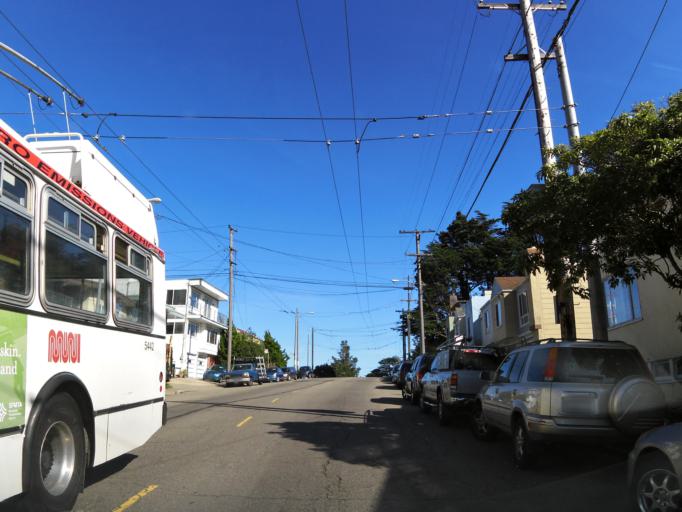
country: US
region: California
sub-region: San Mateo County
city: Daly City
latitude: 37.7489
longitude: -122.4683
